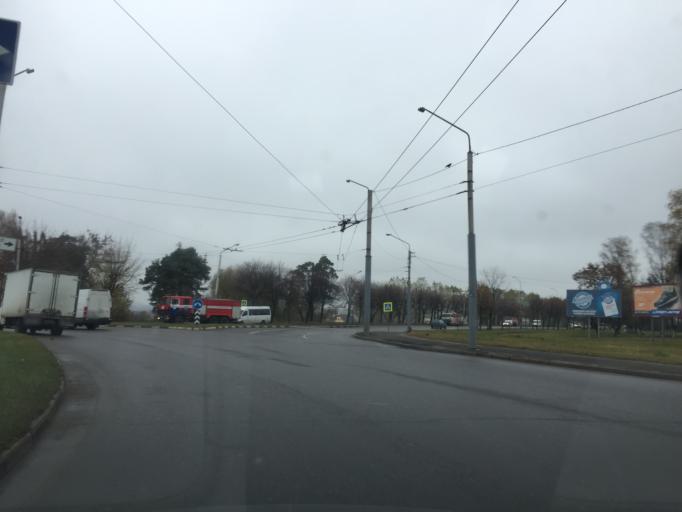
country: BY
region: Mogilev
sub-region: Mahilyowski Rayon
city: Veyno
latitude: 53.8640
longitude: 30.3591
